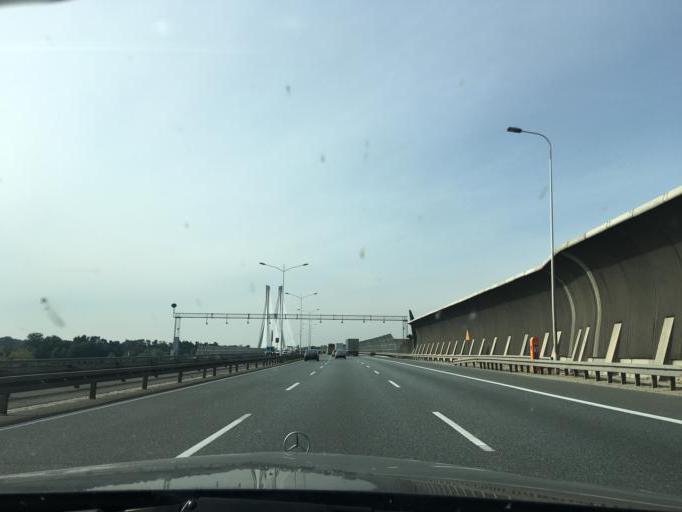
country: PL
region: Lower Silesian Voivodeship
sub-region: Powiat trzebnicki
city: Psary
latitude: 51.1632
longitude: 16.9708
